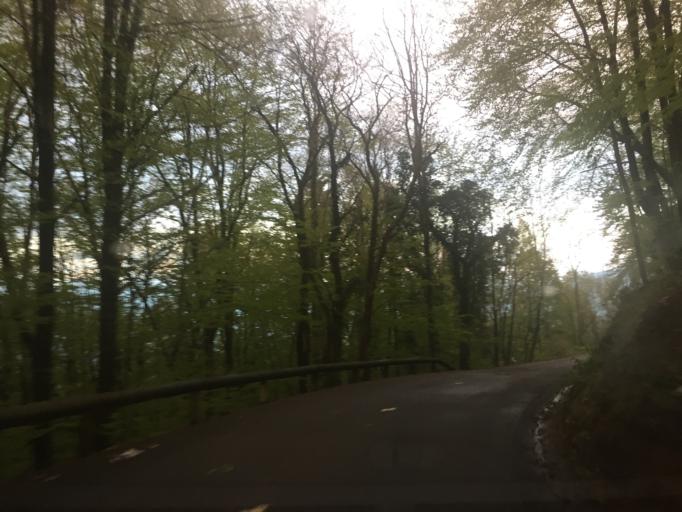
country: FR
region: Rhone-Alpes
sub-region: Departement de la Savoie
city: La Motte-Servolex
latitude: 45.5811
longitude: 5.8308
